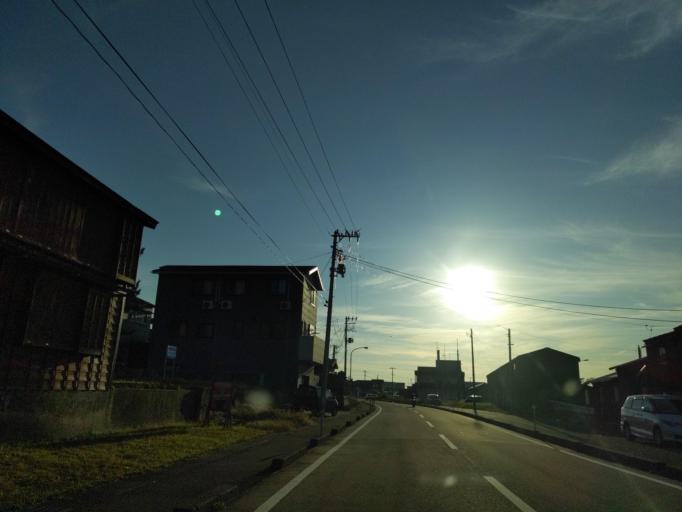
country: JP
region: Niigata
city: Nagaoka
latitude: 37.5410
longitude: 138.6842
